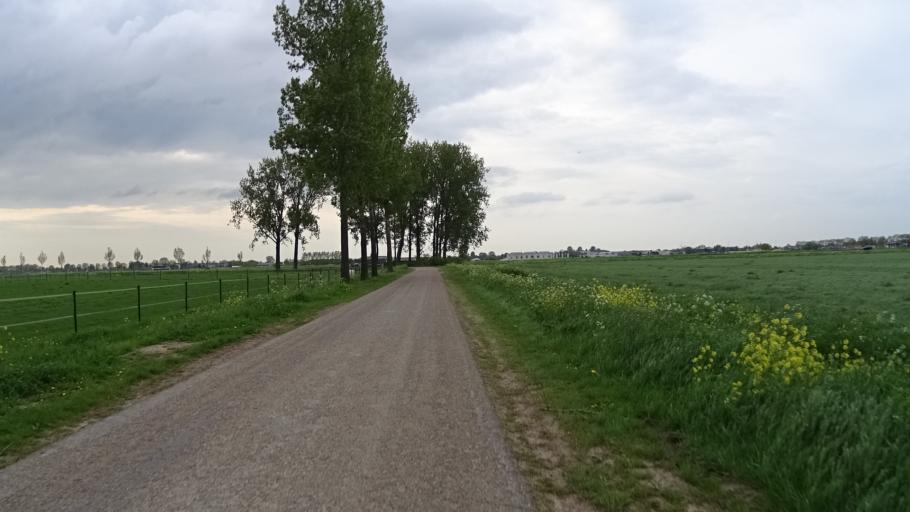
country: NL
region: North Brabant
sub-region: Gemeente Aalburg
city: Aalburg
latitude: 51.7651
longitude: 5.0981
